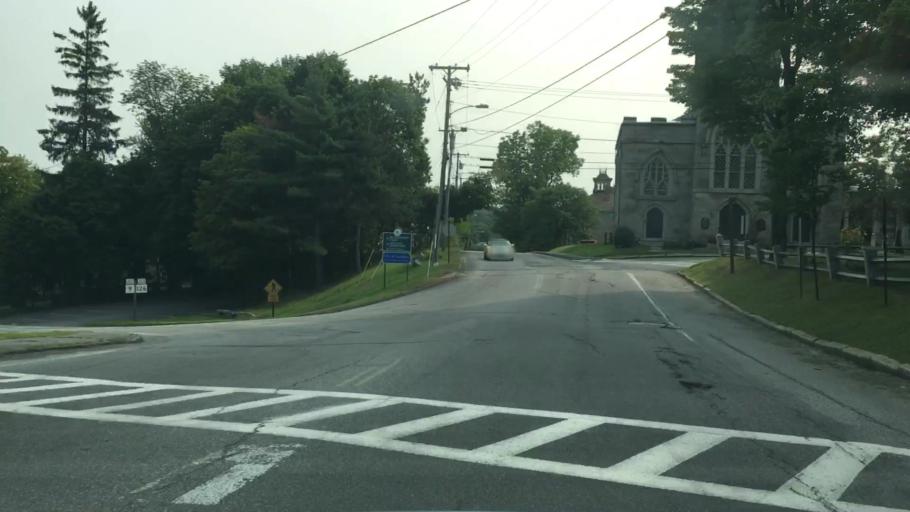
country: US
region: Maine
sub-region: Kennebec County
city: Gardiner
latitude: 44.2274
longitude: -69.7755
